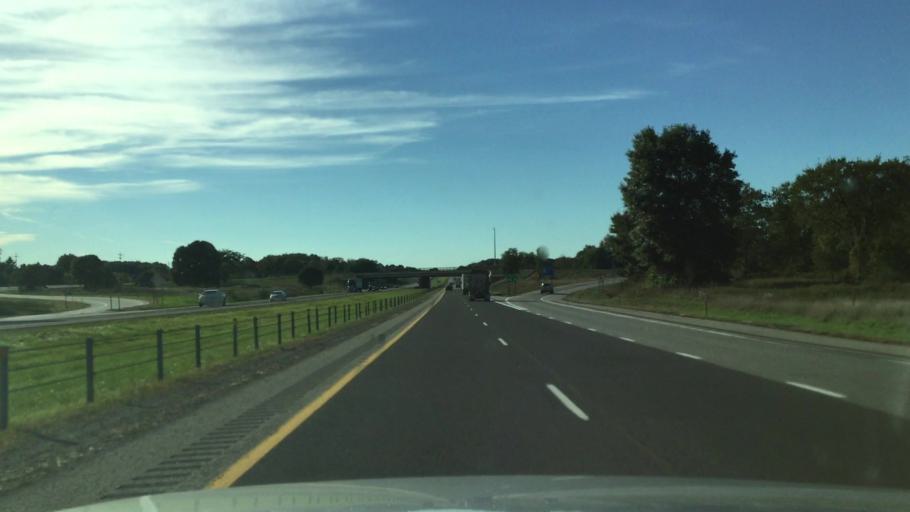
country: US
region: Michigan
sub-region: Calhoun County
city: Springfield
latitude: 42.2717
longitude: -85.2904
